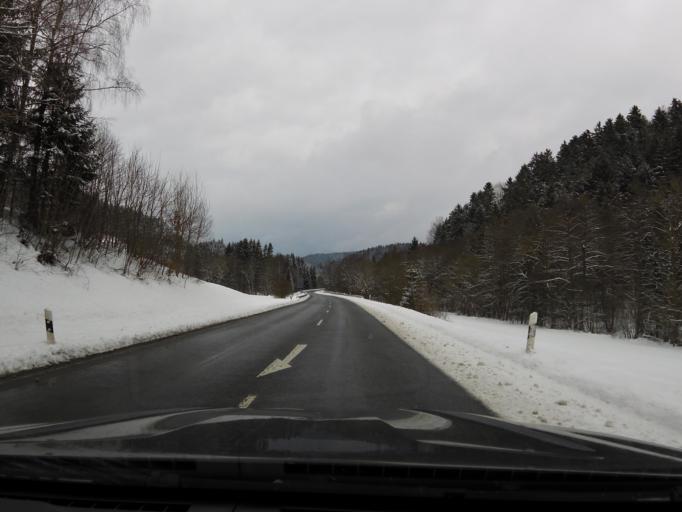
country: DE
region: Bavaria
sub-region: Lower Bavaria
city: Innernzell
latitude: 48.8513
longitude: 13.3076
